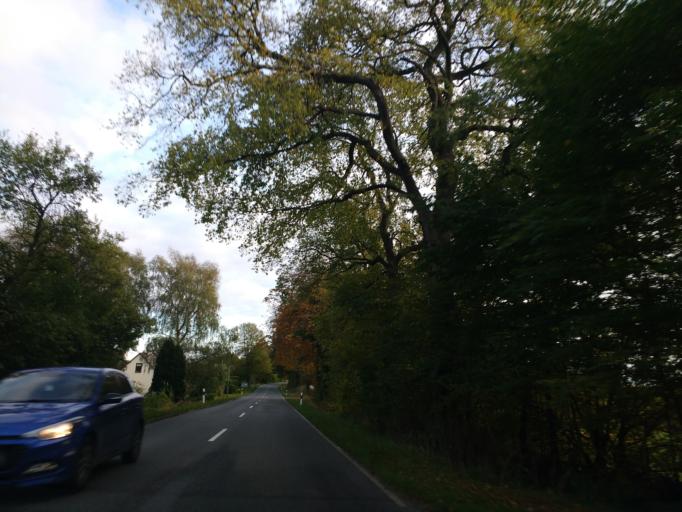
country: DE
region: Schleswig-Holstein
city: Schonwalde am Bungsberg
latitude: 54.2026
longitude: 10.7494
